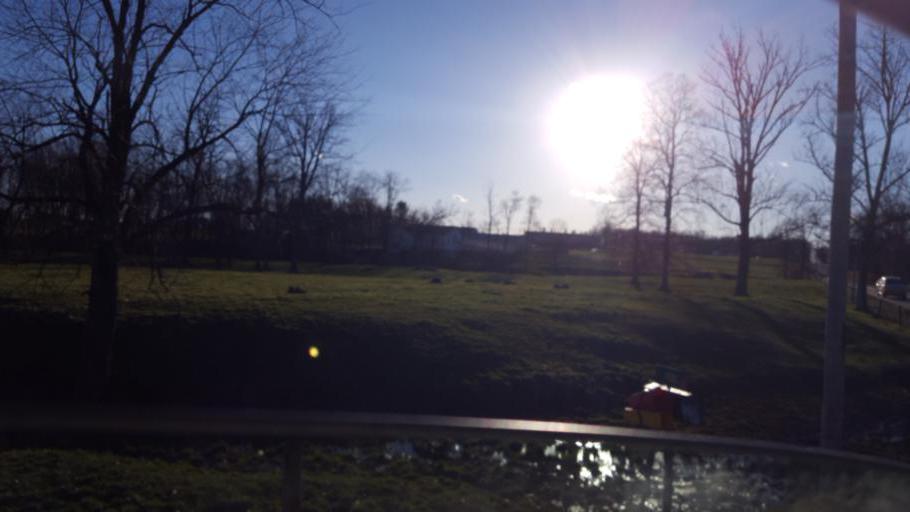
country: US
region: Ohio
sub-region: Wayne County
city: Apple Creek
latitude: 40.6461
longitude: -81.7719
